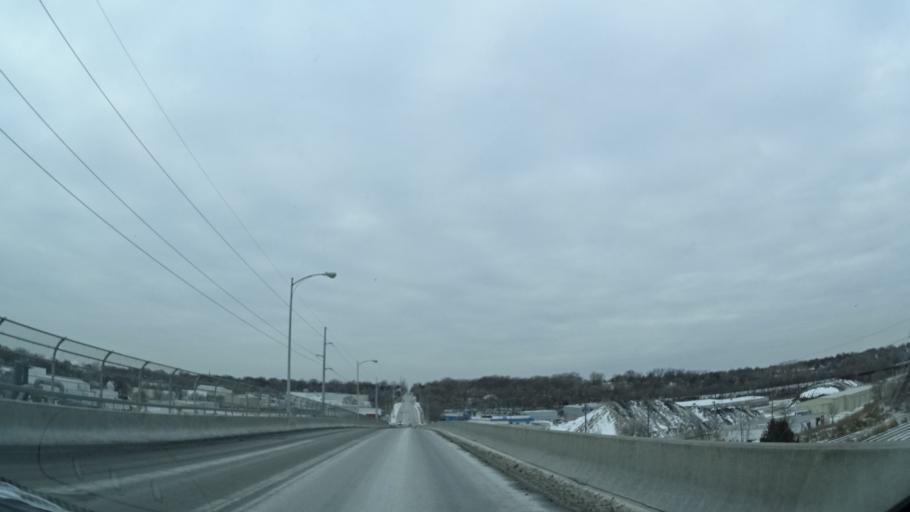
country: US
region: Nebraska
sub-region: Douglas County
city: Omaha
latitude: 41.2197
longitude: -95.9564
